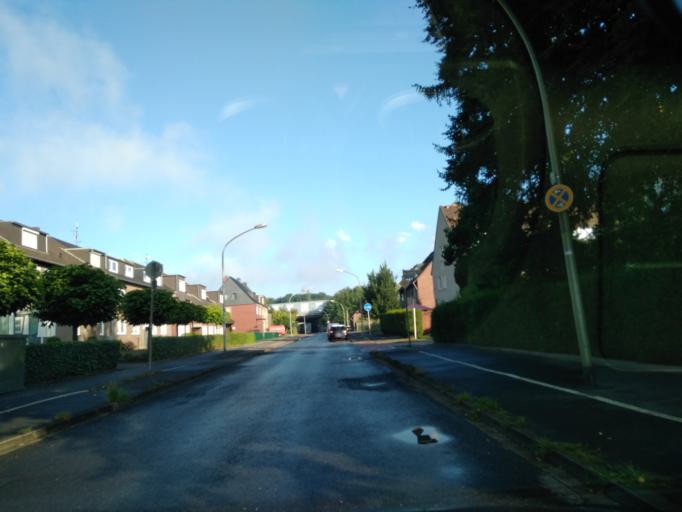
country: DE
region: North Rhine-Westphalia
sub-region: Regierungsbezirk Munster
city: Gelsenkirchen
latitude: 51.5630
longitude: 7.0778
